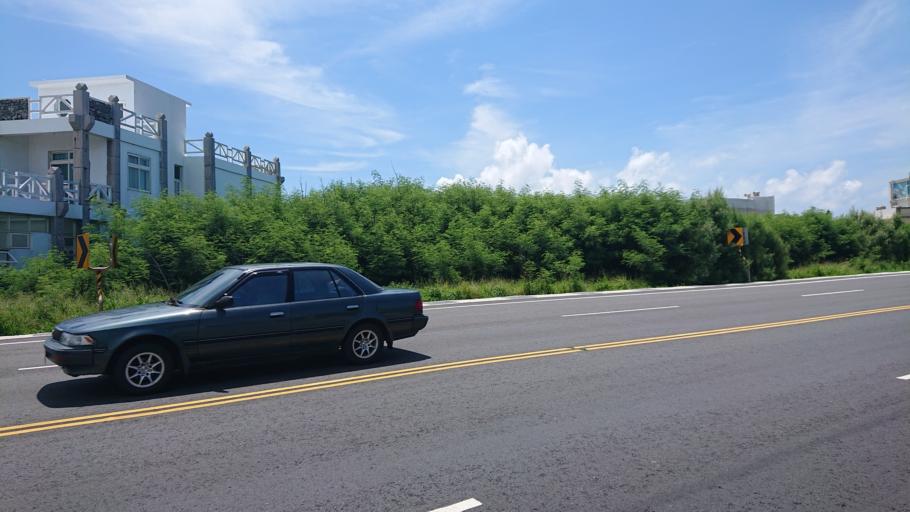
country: TW
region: Taiwan
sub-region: Penghu
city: Ma-kung
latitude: 23.6134
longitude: 119.6082
